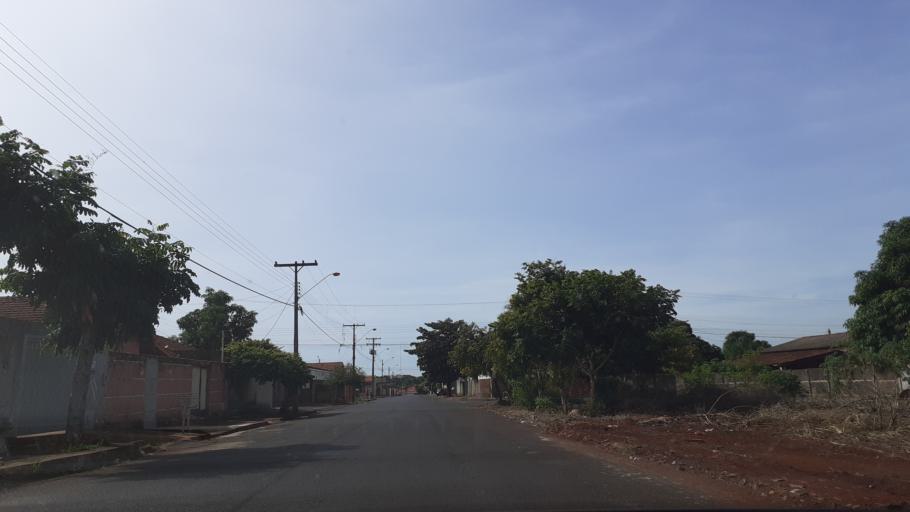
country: BR
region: Goias
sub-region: Itumbiara
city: Itumbiara
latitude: -18.4217
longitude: -49.2440
